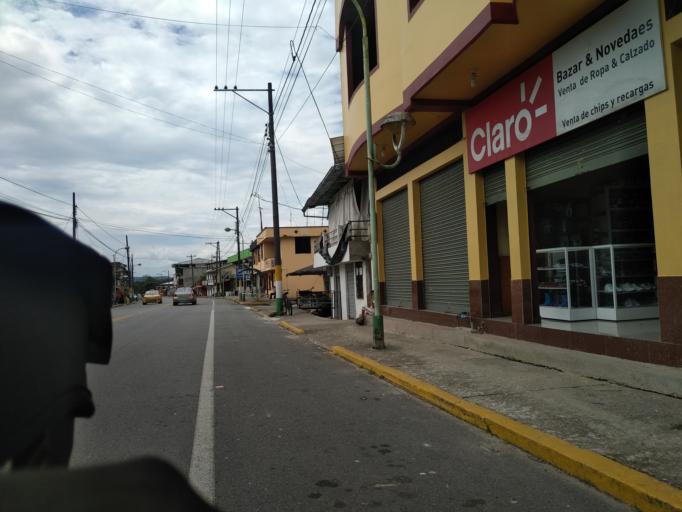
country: EC
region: Napo
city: Tena
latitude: -1.1681
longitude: -77.8555
